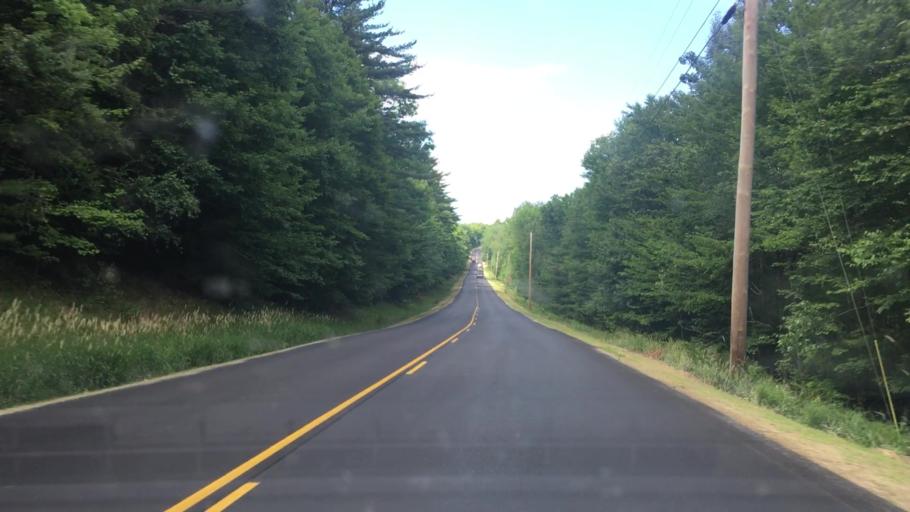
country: US
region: Maine
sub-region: Franklin County
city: Jay
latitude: 44.5405
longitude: -70.1894
